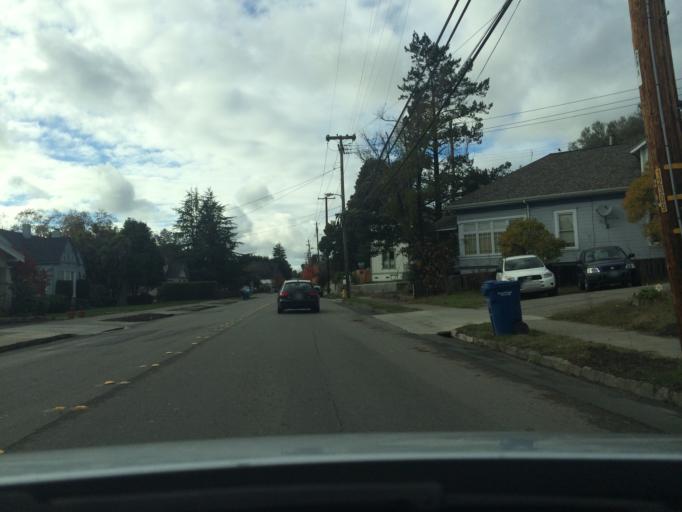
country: US
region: California
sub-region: Sonoma County
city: Petaluma
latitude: 38.2343
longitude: -122.6485
